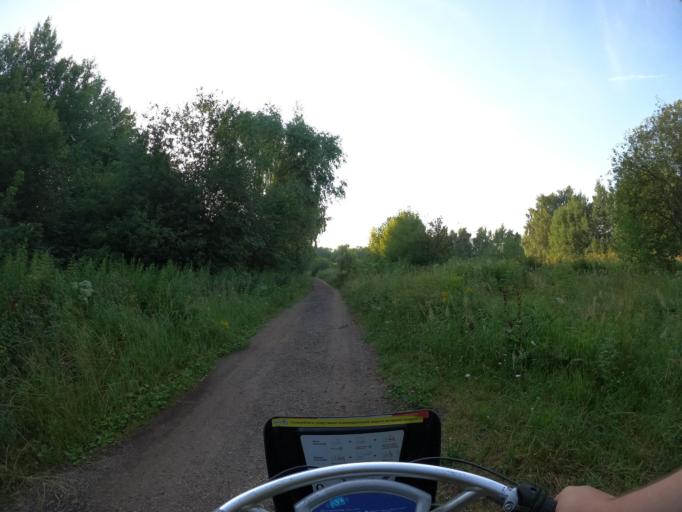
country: RU
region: Moscow
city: Strogino
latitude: 55.8238
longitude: 37.4057
